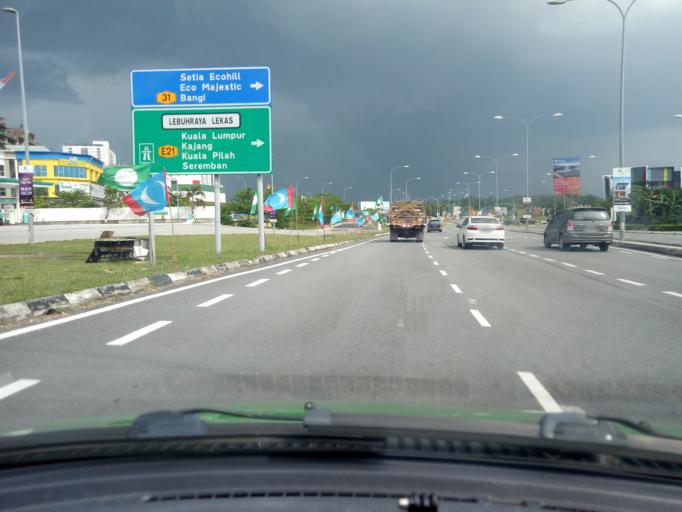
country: MY
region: Selangor
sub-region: Hulu Langat
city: Semenyih
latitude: 2.9287
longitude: 101.8567
